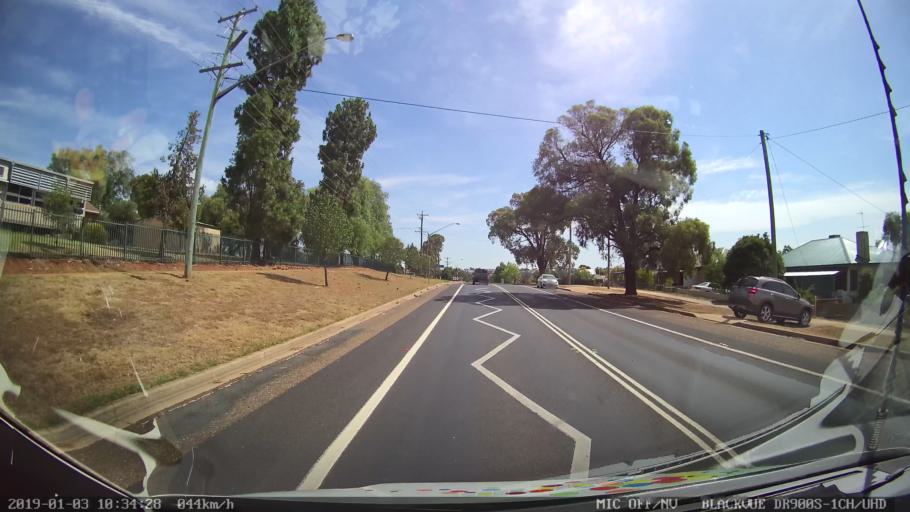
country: AU
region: New South Wales
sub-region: Young
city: Young
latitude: -34.3216
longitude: 148.2914
